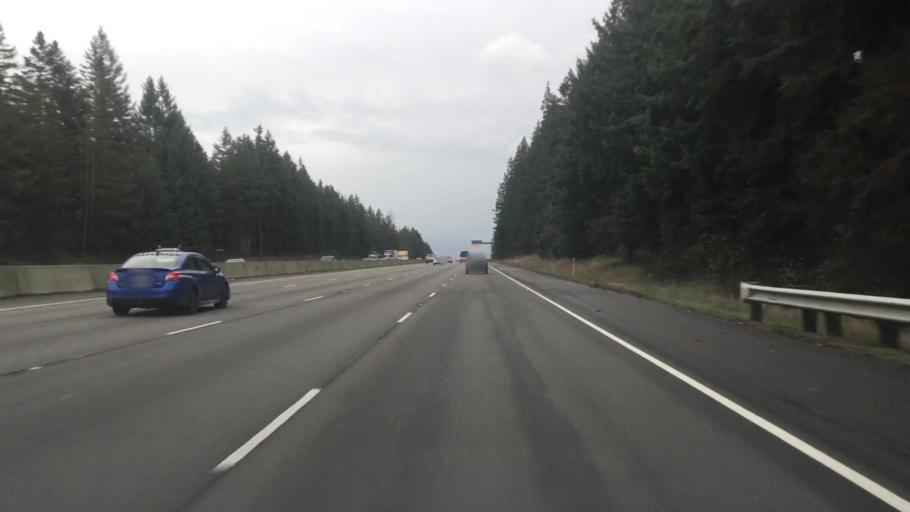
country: US
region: Washington
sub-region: Thurston County
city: Grand Mound
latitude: 46.8848
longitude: -122.9648
